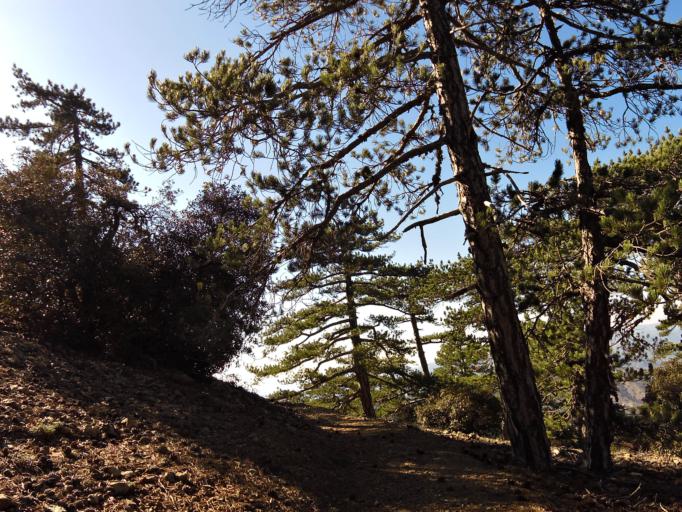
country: CY
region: Lefkosia
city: Kakopetria
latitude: 34.9575
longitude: 32.8531
